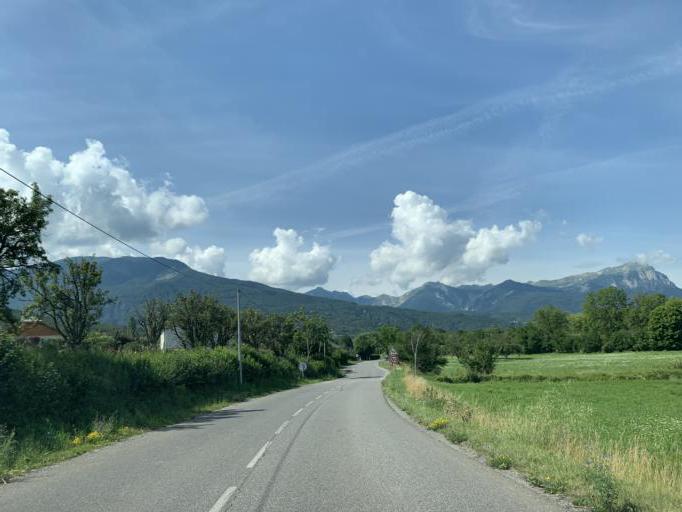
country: FR
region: Provence-Alpes-Cote d'Azur
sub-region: Departement des Hautes-Alpes
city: Embrun
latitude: 44.5496
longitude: 6.5014
